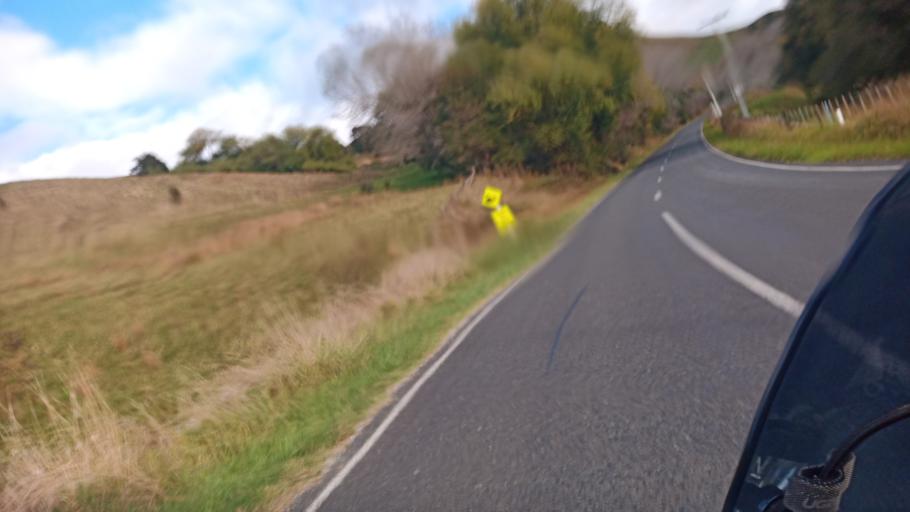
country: NZ
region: Gisborne
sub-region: Gisborne District
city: Gisborne
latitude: -38.5938
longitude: 177.7749
